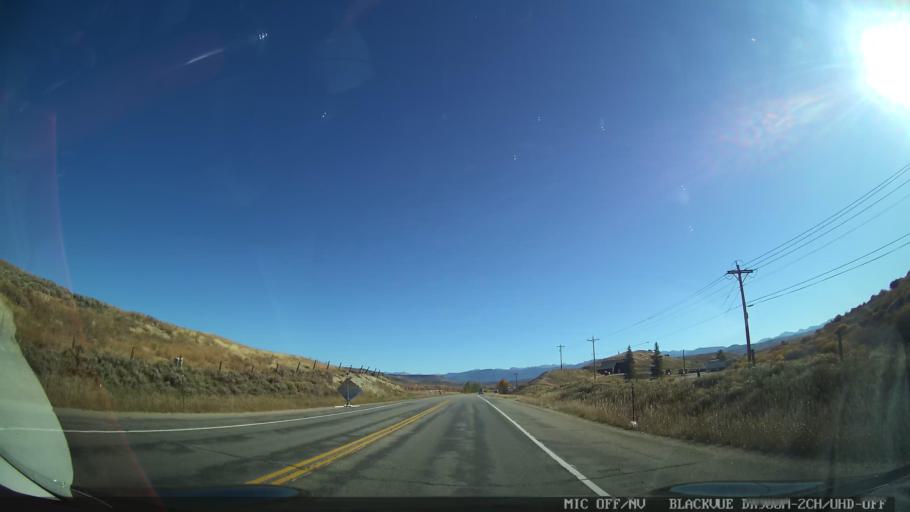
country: US
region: Colorado
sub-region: Grand County
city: Granby
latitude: 40.0990
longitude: -105.9507
